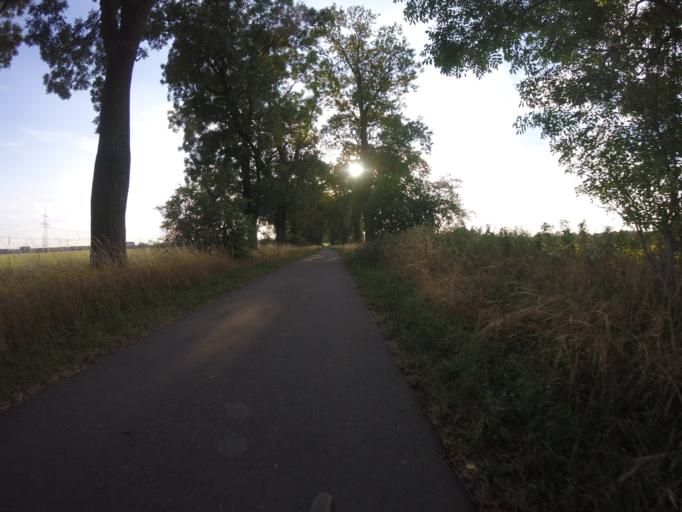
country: DE
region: Brandenburg
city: Altlandsberg
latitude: 52.5765
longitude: 13.6898
